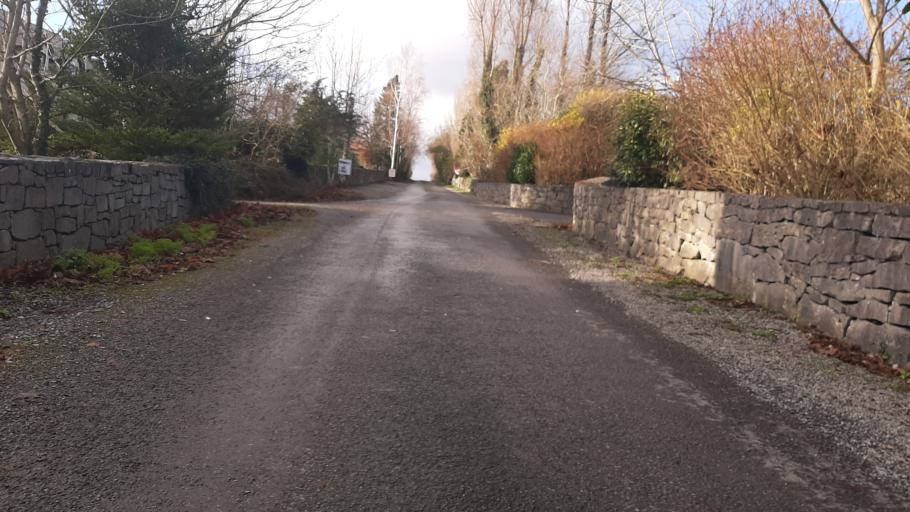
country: IE
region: Connaught
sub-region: County Galway
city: Gaillimh
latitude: 53.3027
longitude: -9.0632
